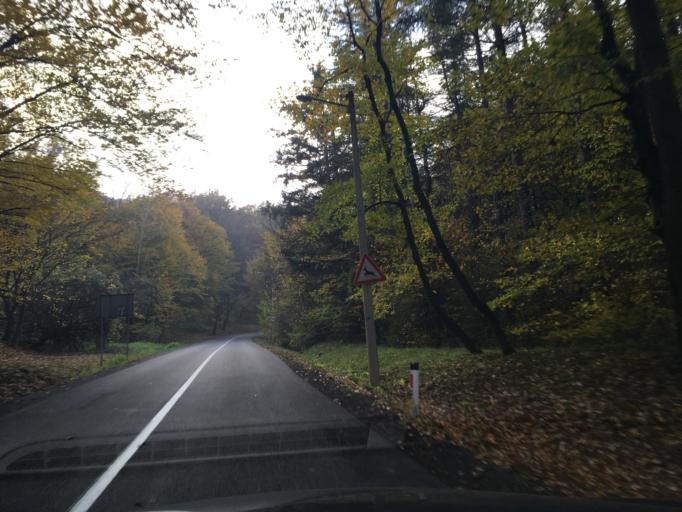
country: RS
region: Central Serbia
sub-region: Belgrade
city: Sopot
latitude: 44.4729
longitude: 20.5656
